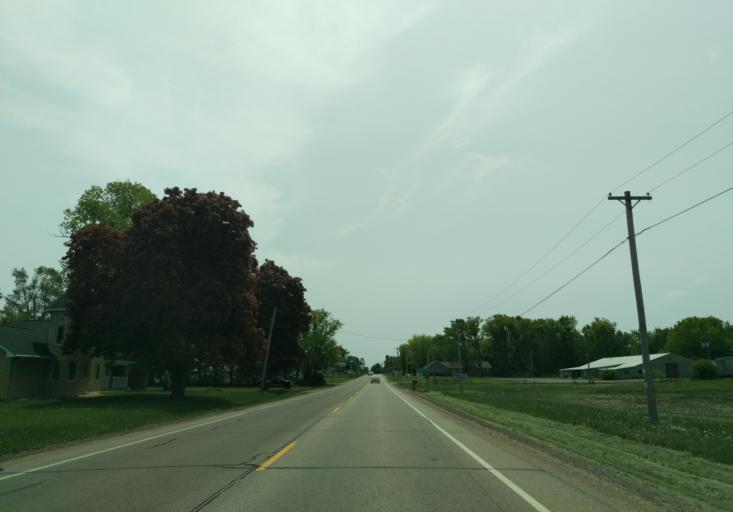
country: US
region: Wisconsin
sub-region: Rock County
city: Evansville
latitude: 42.7922
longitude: -89.2992
